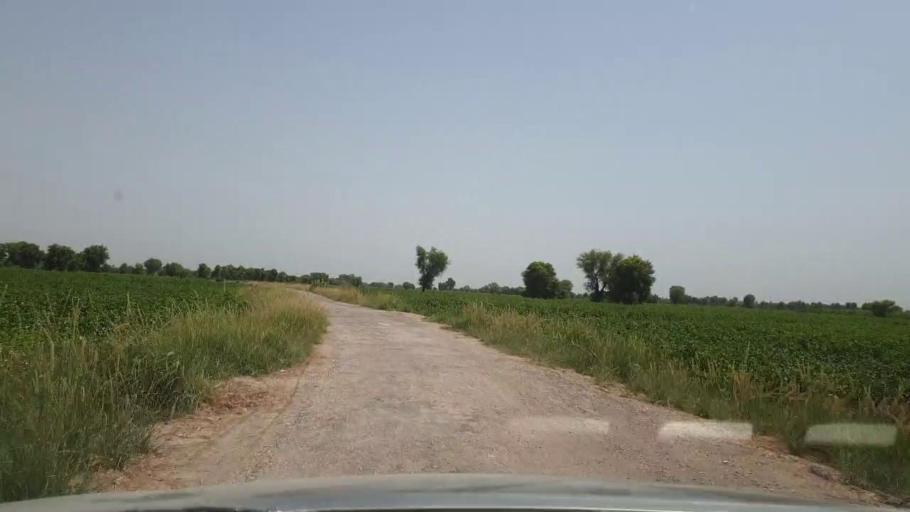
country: PK
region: Sindh
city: Pano Aqil
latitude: 27.8043
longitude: 69.2403
